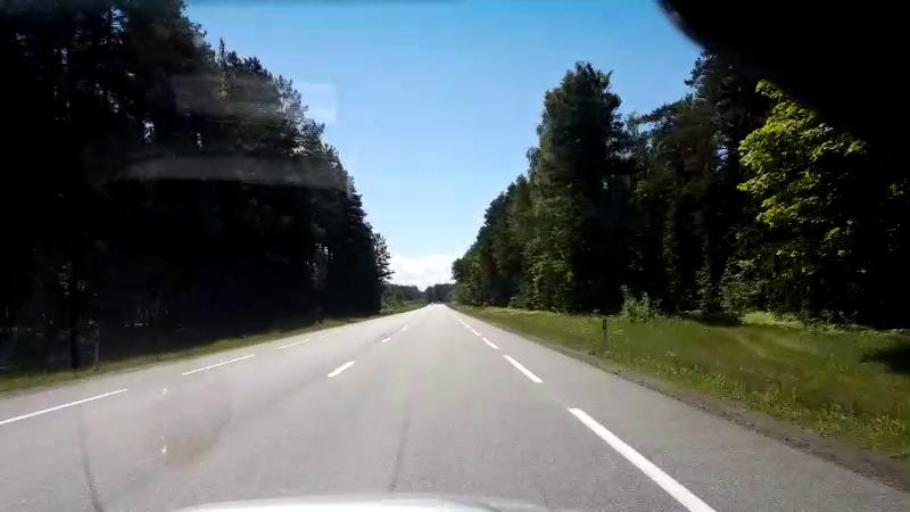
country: LV
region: Saulkrastu
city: Saulkrasti
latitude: 57.4452
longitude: 24.4294
